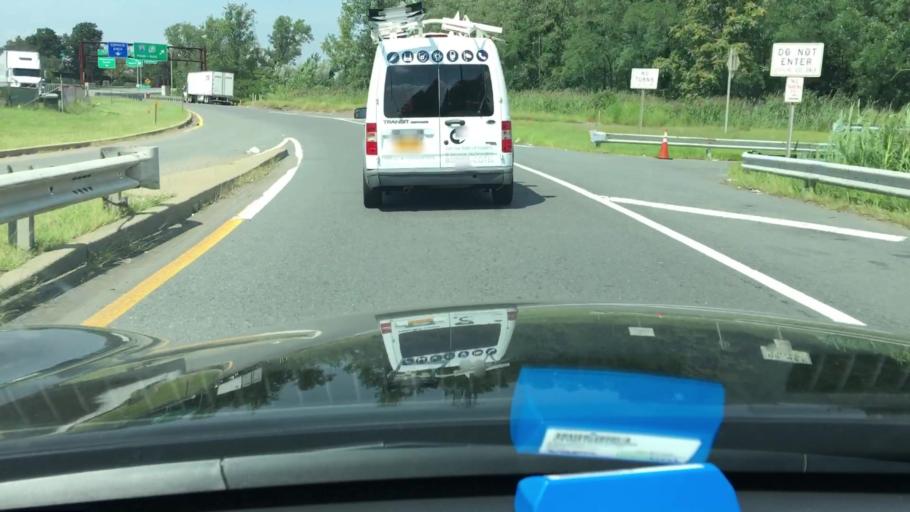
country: US
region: New Jersey
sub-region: Bergen County
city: Ridgefield
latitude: 40.8238
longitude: -74.0281
